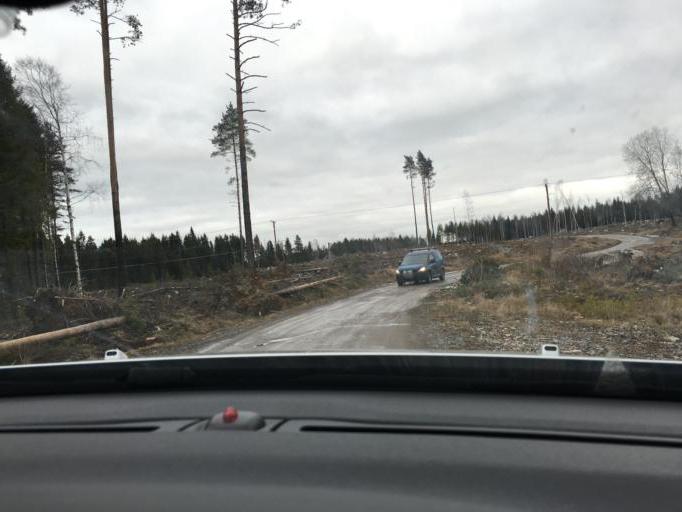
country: SE
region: Soedermanland
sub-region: Katrineholms Kommun
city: Katrineholm
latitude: 58.9948
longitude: 16.2637
